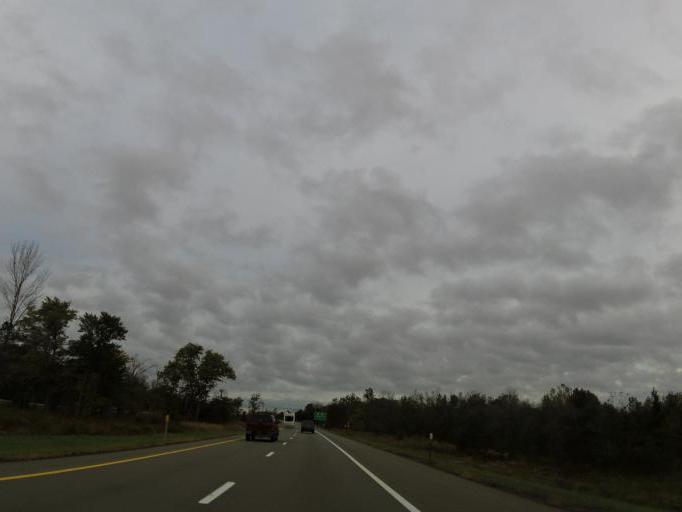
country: US
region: New York
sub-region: Erie County
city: Elma Center
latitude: 42.8282
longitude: -78.6749
